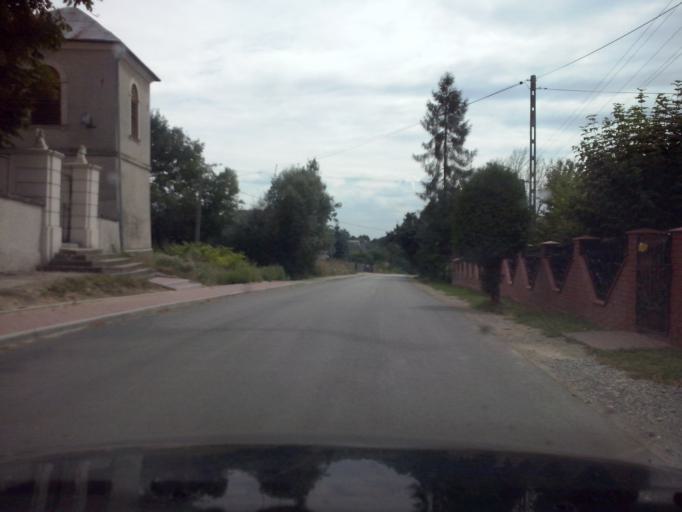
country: PL
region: Swietokrzyskie
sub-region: Powiat kielecki
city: Lagow
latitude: 50.7252
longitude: 21.1063
